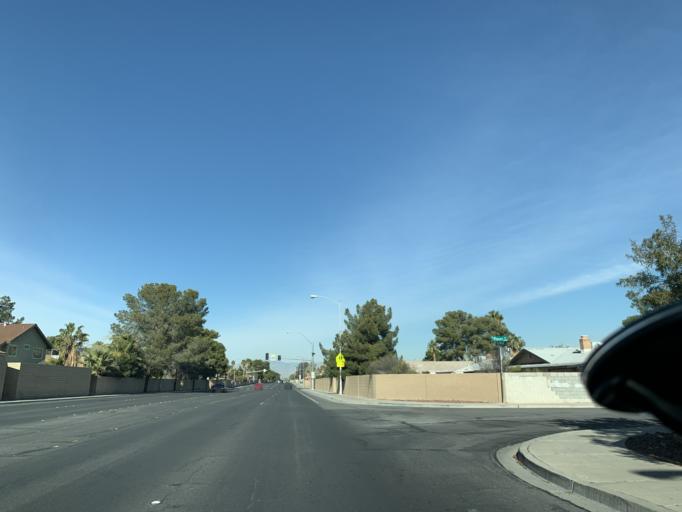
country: US
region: Nevada
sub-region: Clark County
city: Spring Valley
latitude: 36.1057
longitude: -115.2339
